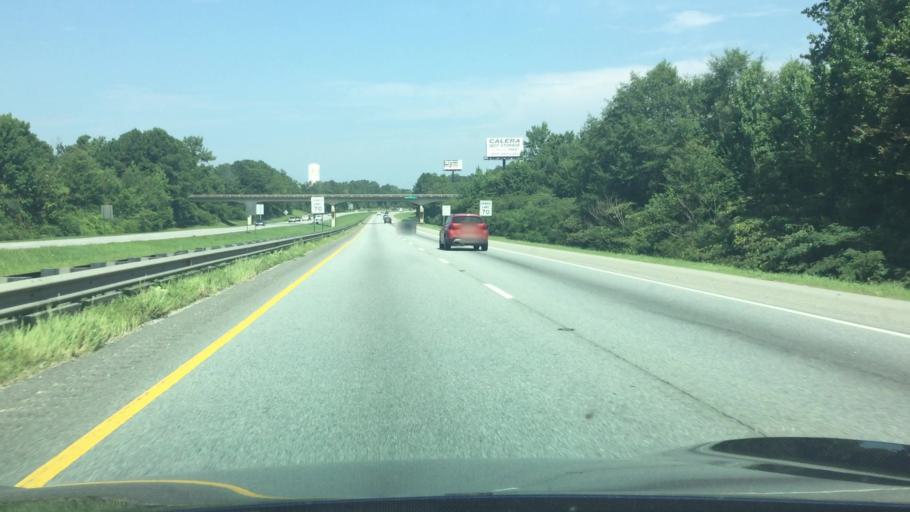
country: US
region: Alabama
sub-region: Shelby County
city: Calera
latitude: 33.1497
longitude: -86.7605
